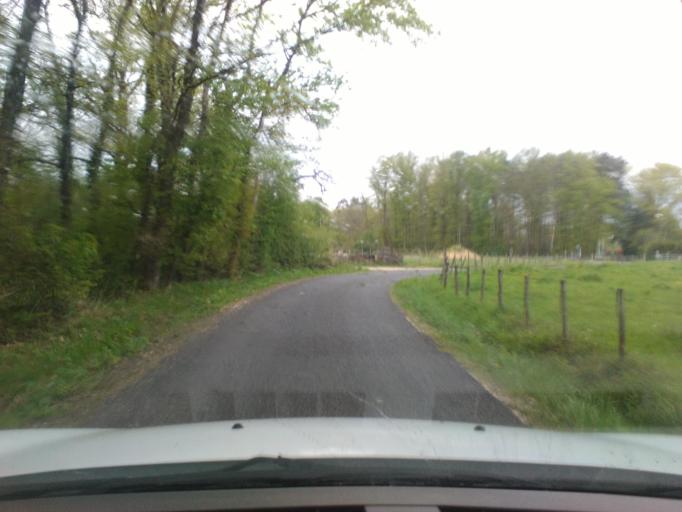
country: FR
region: Rhone-Alpes
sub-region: Departement de l'Ain
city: Saint-Etienne-du-Bois
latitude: 46.2604
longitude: 5.2816
